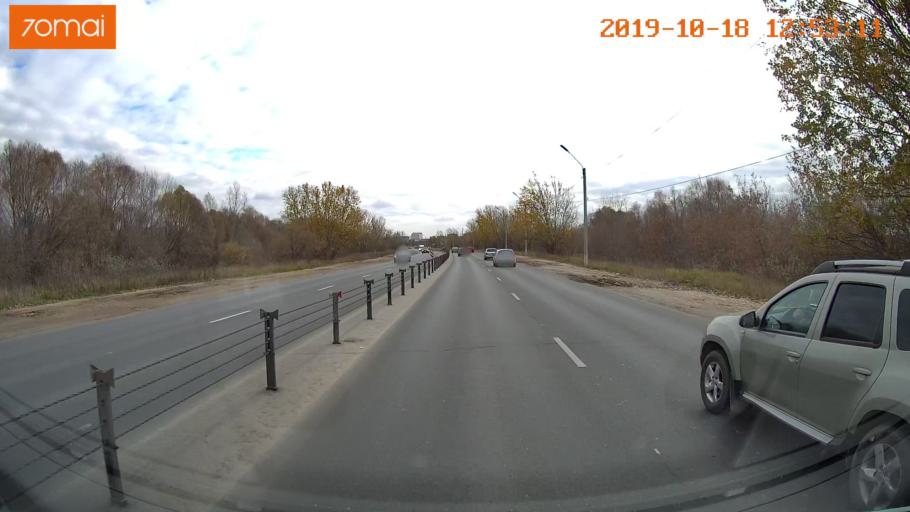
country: RU
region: Rjazan
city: Ryazan'
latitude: 54.6463
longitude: 39.7031
